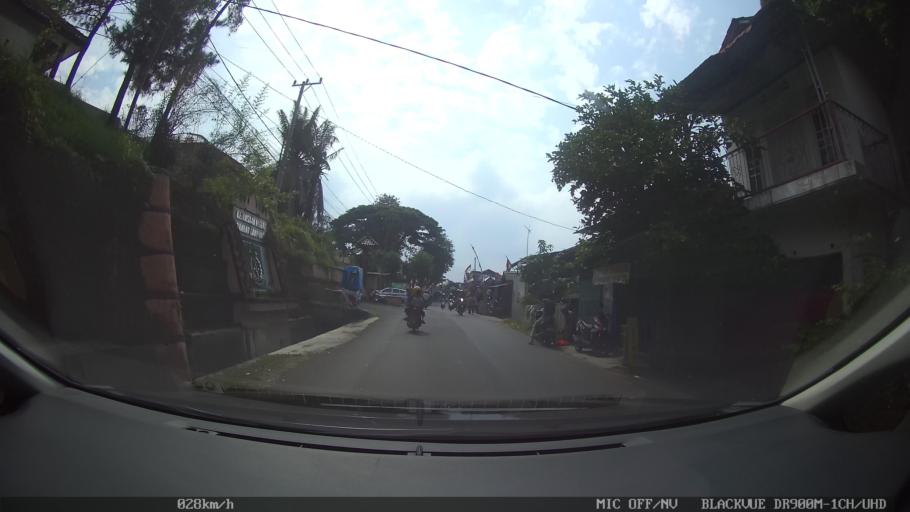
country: ID
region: Lampung
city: Bandarlampung
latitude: -5.4453
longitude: 105.2581
